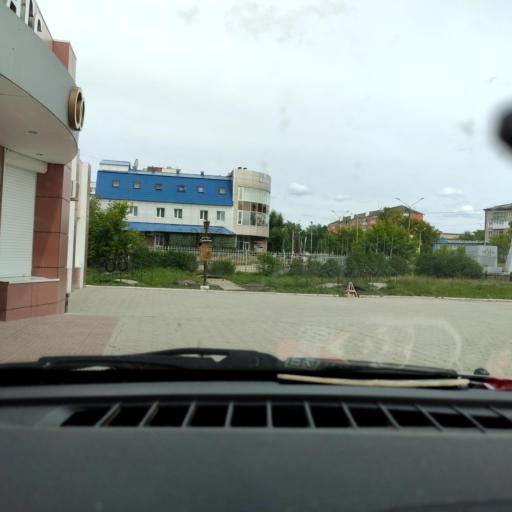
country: RU
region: Perm
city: Chusovoy
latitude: 58.2729
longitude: 57.8110
